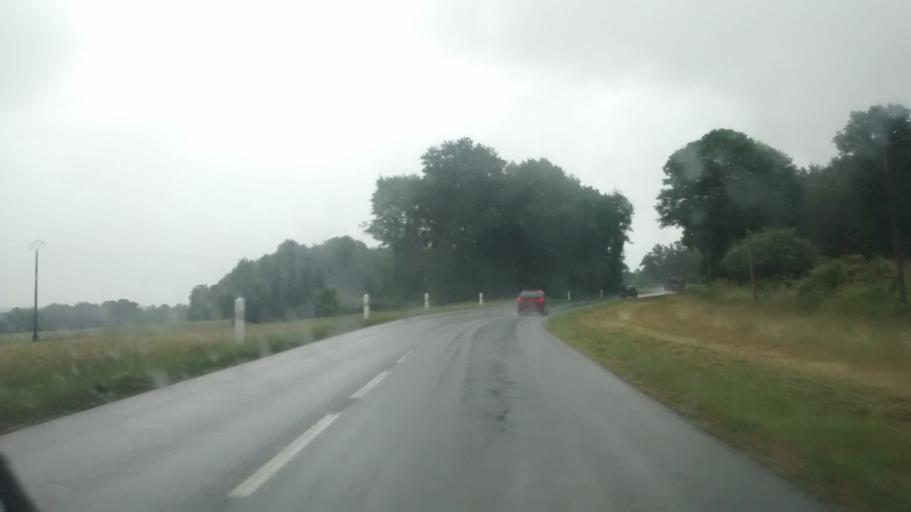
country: FR
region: Brittany
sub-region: Departement du Morbihan
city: La Gacilly
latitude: 47.7820
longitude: -2.1778
